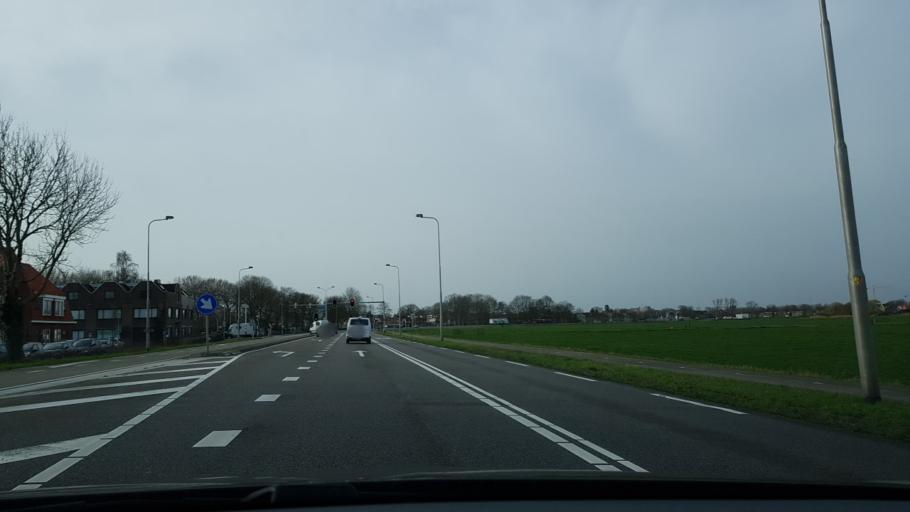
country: NL
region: North Holland
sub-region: Gemeente Ouder-Amstel
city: Ouderkerk aan de Amstel
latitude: 52.3007
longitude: 4.9135
